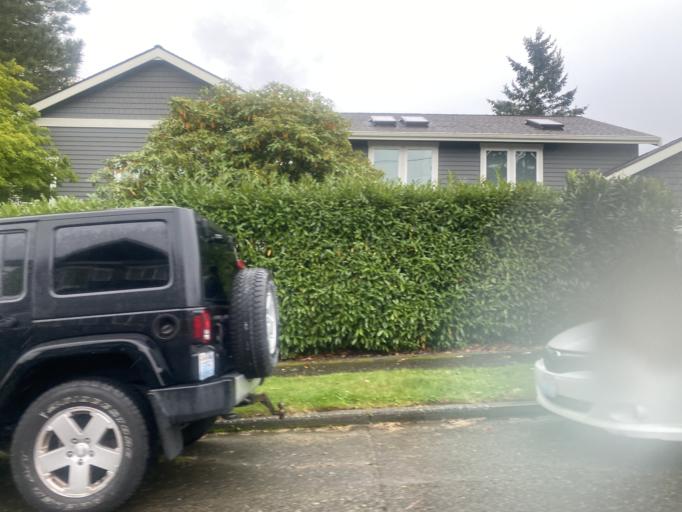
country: US
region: Washington
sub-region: King County
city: Seattle
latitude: 47.6423
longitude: -122.3920
